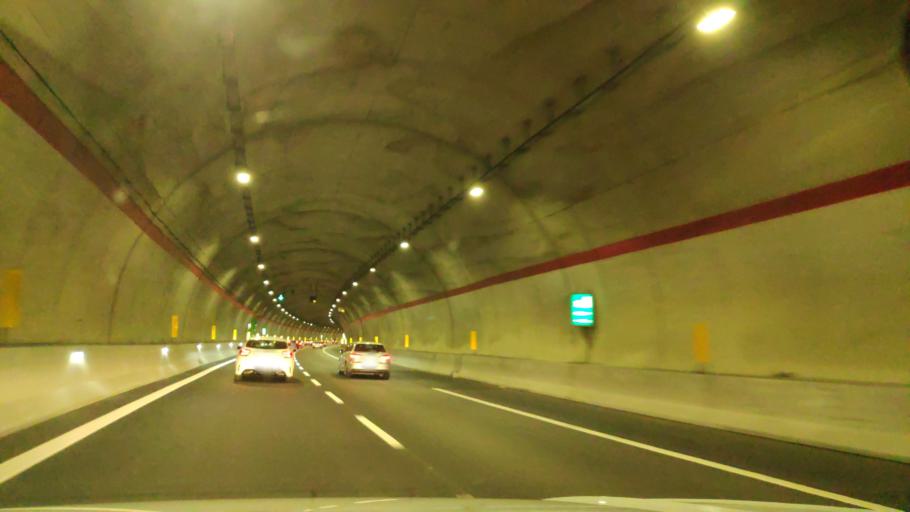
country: IT
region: Calabria
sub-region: Provincia di Cosenza
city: Mormanno
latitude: 39.8870
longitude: 15.9826
